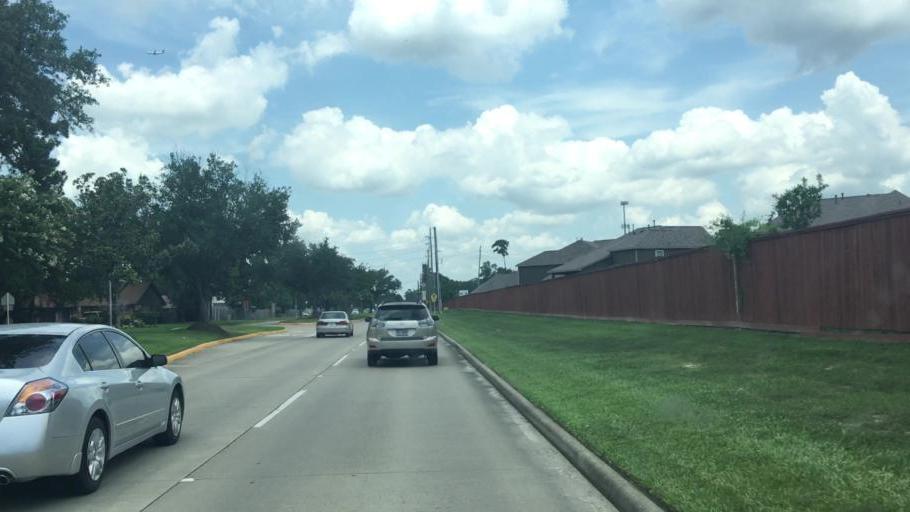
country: US
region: Texas
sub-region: Harris County
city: Atascocita
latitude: 29.9755
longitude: -95.2123
